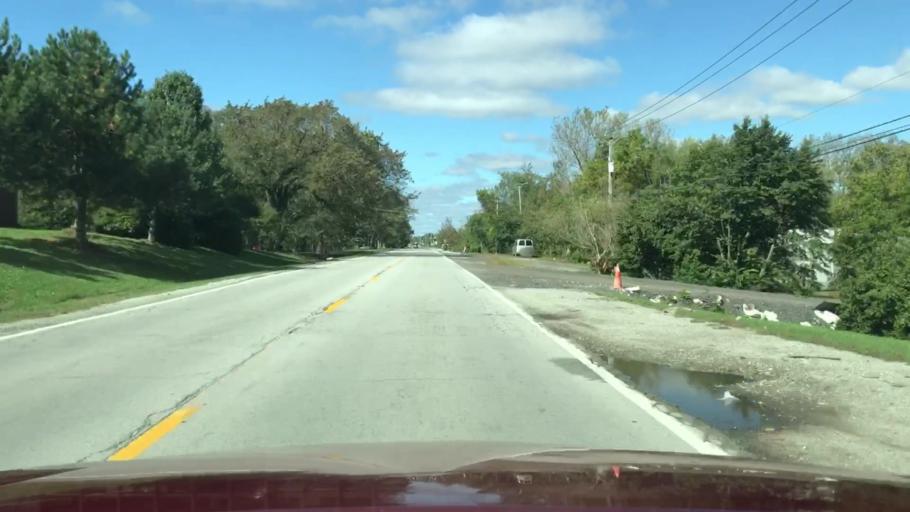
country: US
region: Illinois
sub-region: Cook County
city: Ford Heights
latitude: 41.5293
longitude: -87.5721
